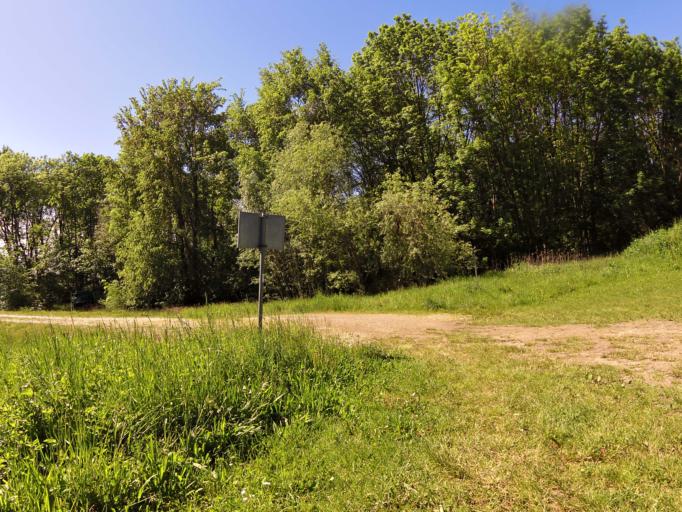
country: DE
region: Bavaria
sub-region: Upper Bavaria
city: Moosburg
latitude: 48.4541
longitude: 11.9378
